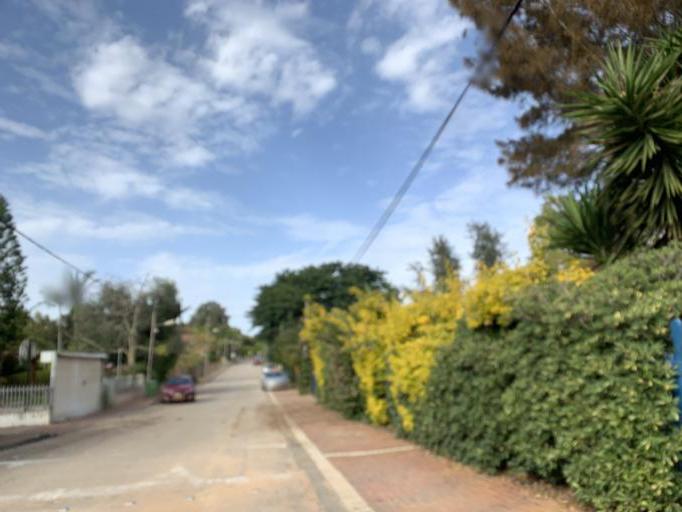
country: IL
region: Central District
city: Hod HaSharon
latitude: 32.1513
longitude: 34.9029
